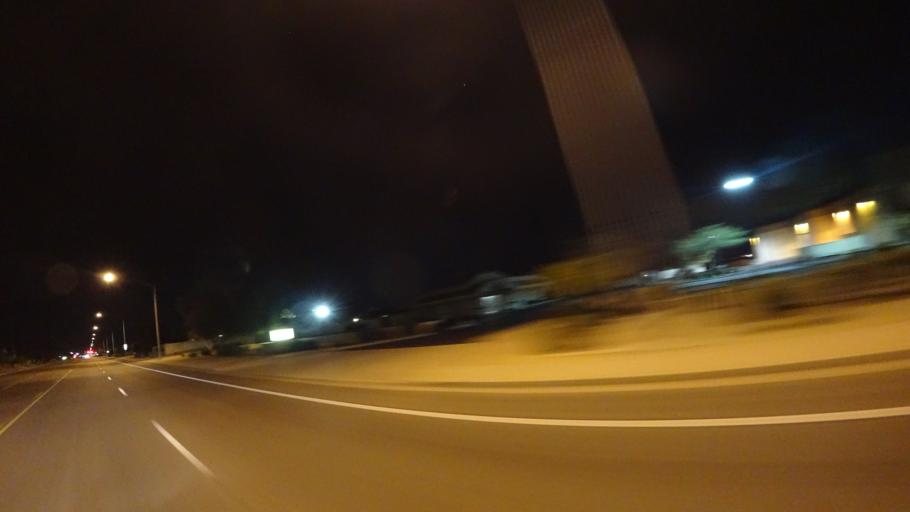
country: US
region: Arizona
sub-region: Maricopa County
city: Gilbert
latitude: 33.4374
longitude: -111.6996
